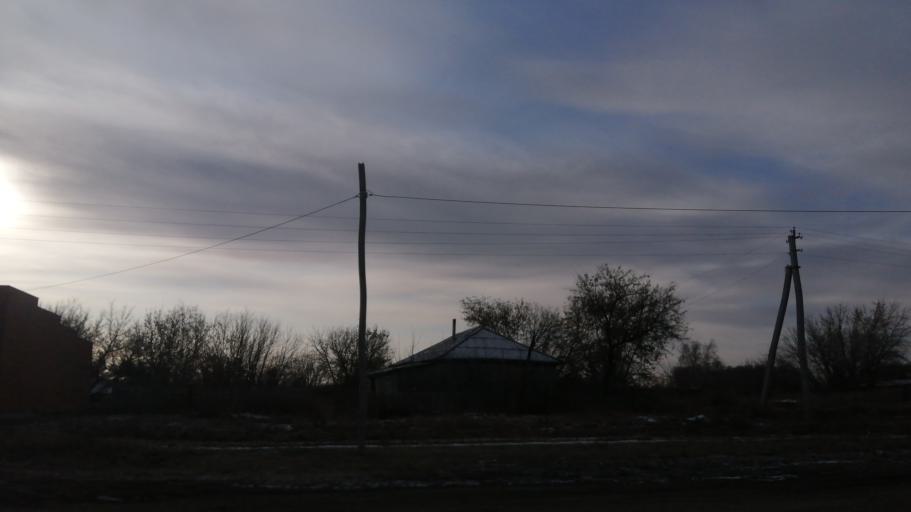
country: RU
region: Novosibirsk
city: Krasnozerskoye
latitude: 53.9854
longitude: 78.7069
